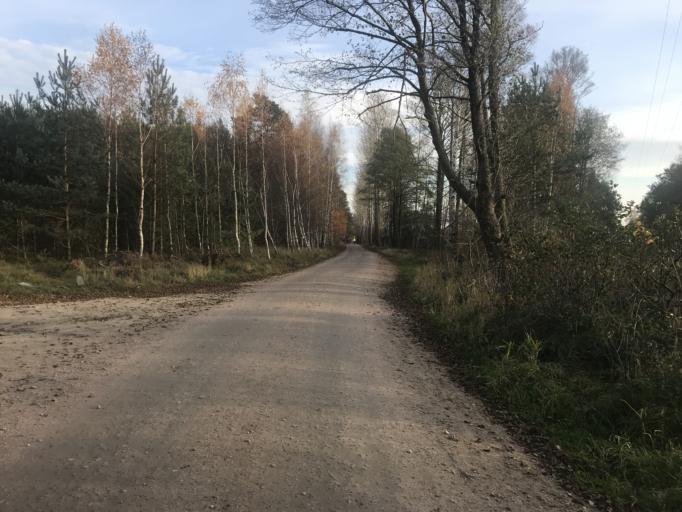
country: PL
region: Pomeranian Voivodeship
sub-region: Powiat pucki
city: Wierzchucino
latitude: 54.8210
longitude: 17.9505
